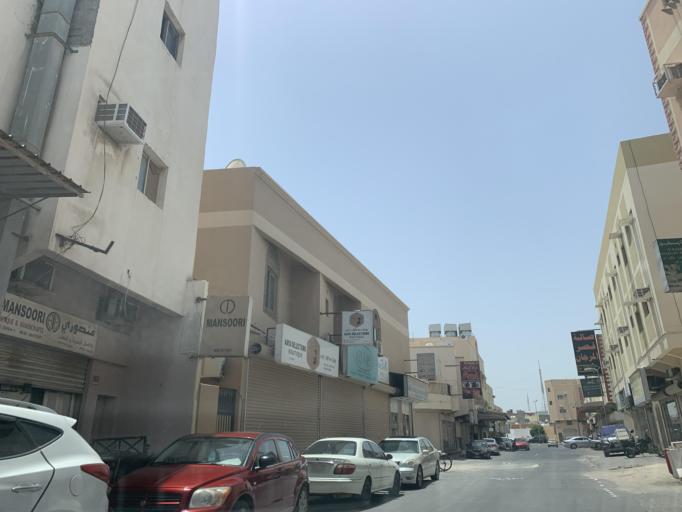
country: BH
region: Northern
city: Madinat `Isa
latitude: 26.1686
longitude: 50.5688
